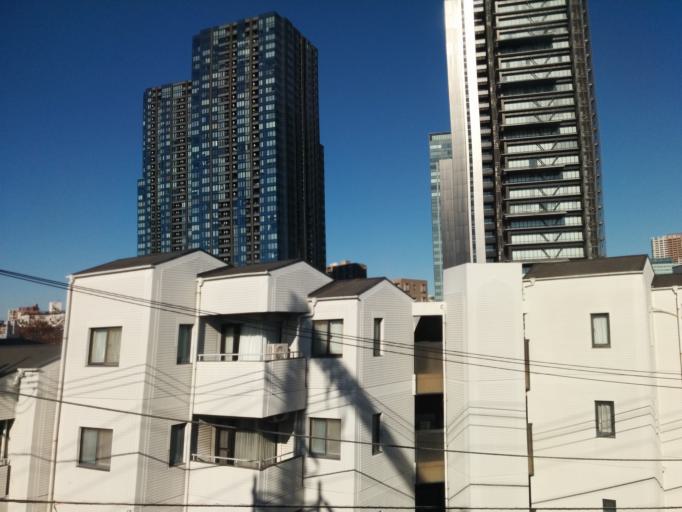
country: JP
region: Tokyo
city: Tokyo
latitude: 35.6152
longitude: 139.7296
